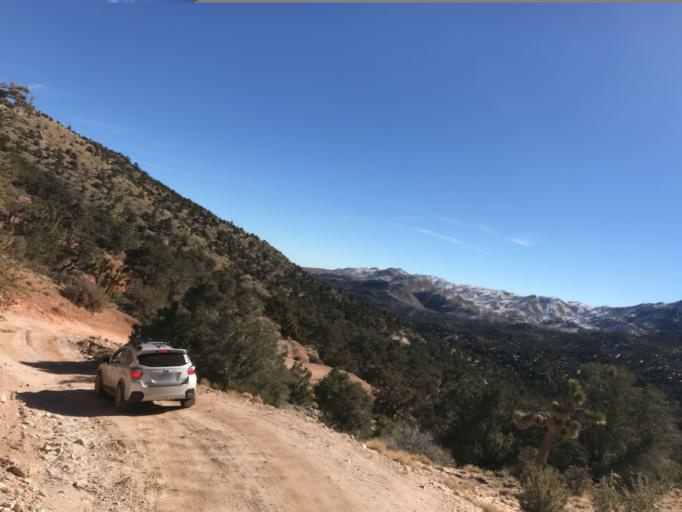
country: US
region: California
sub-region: San Bernardino County
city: Big Bear City
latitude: 34.2397
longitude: -116.6913
